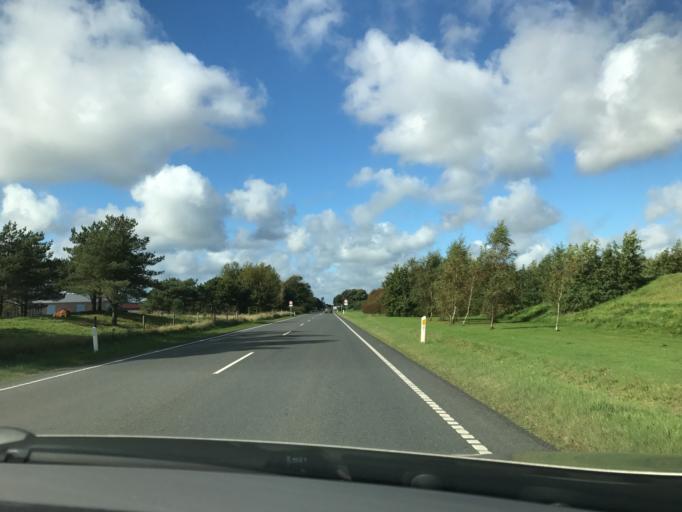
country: DK
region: South Denmark
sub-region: Billund Kommune
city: Billund
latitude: 55.7234
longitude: 9.1434
